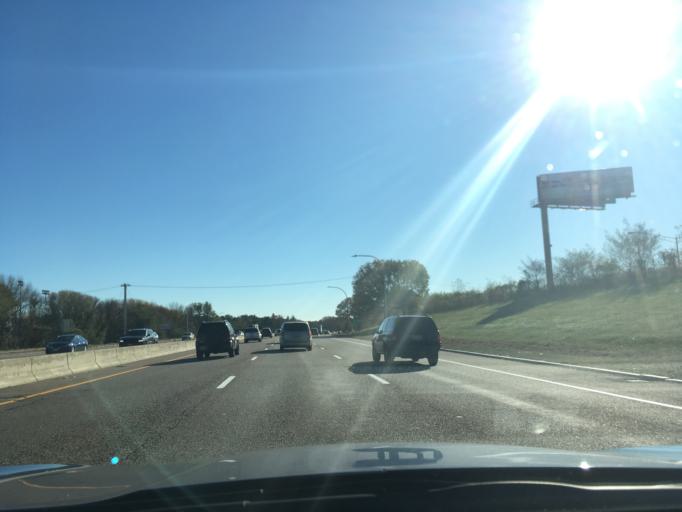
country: US
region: Rhode Island
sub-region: Providence County
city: Pawtucket
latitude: 41.8609
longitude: -71.4045
